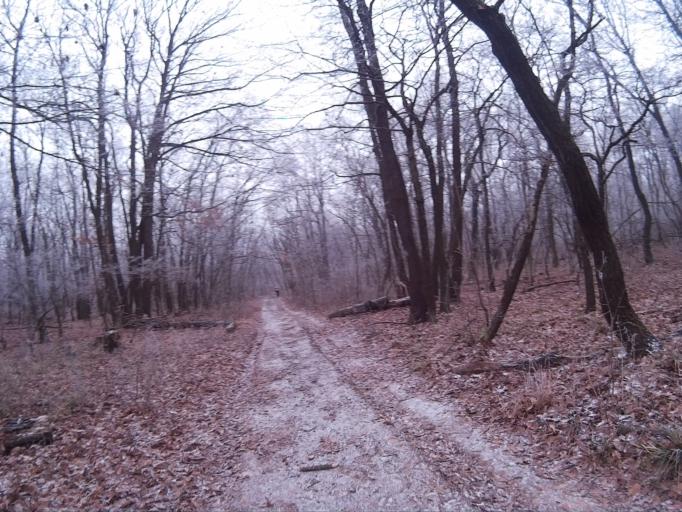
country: HU
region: Fejer
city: Csakvar
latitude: 47.3861
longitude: 18.4208
